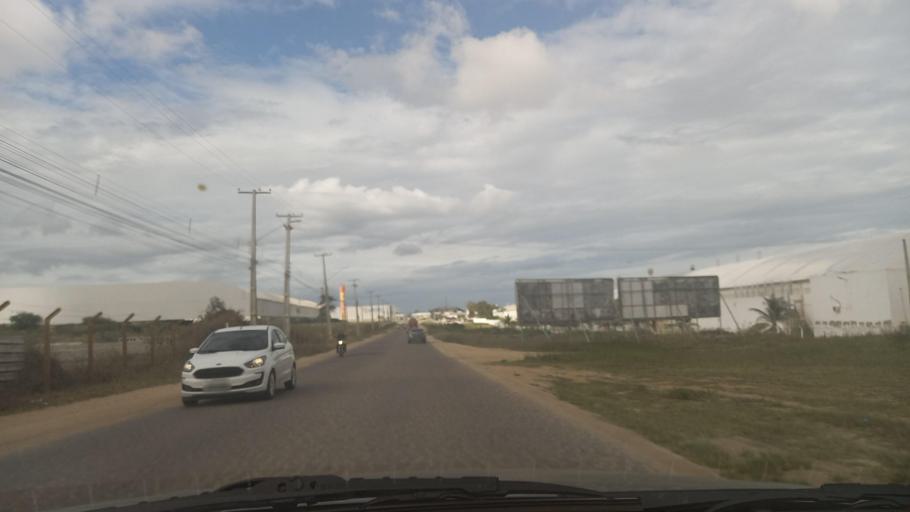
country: BR
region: Pernambuco
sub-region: Caruaru
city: Caruaru
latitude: -8.2897
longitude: -36.0169
